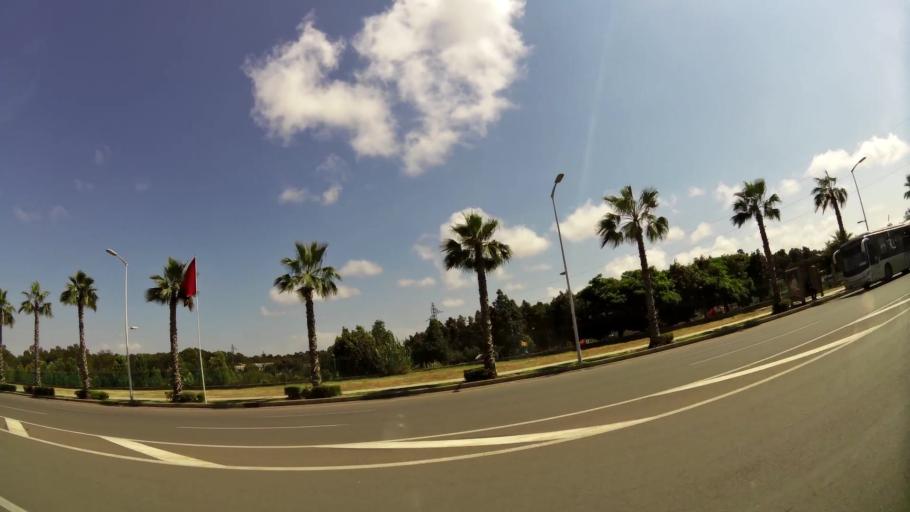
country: MA
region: Rabat-Sale-Zemmour-Zaer
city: Sale
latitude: 34.0350
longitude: -6.7921
